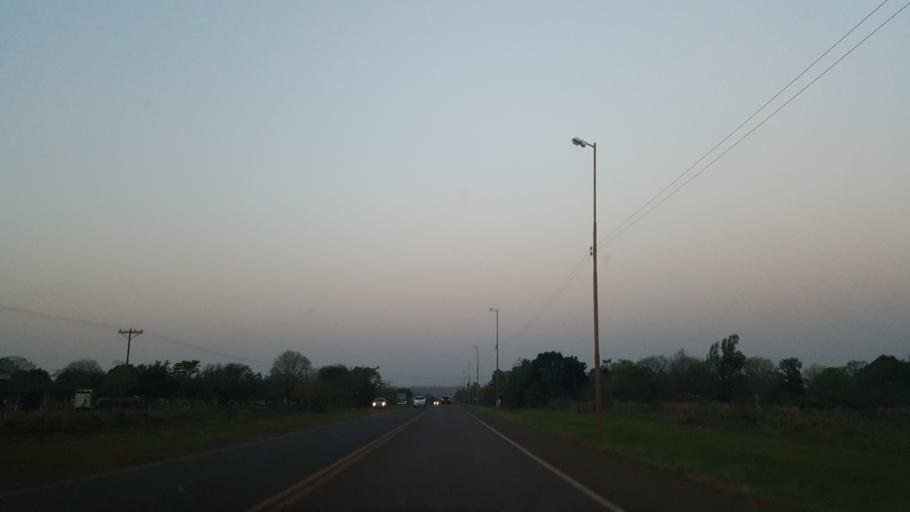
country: AR
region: Misiones
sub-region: Departamento de Capital
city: Posadas
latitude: -27.4063
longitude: -55.9726
